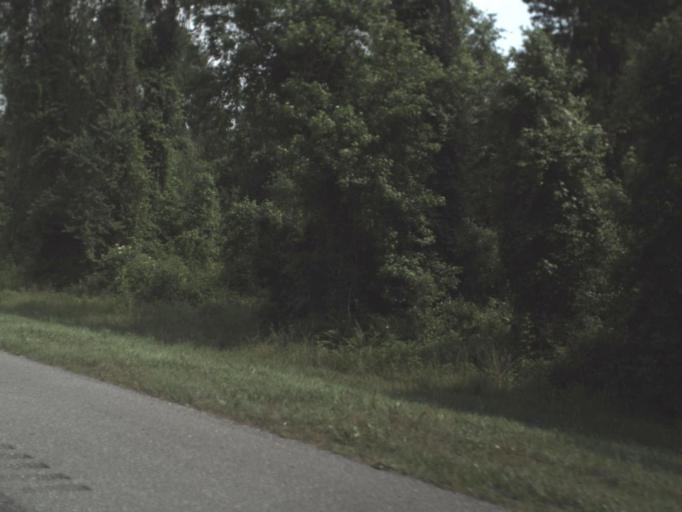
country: US
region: Florida
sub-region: Suwannee County
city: Live Oak
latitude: 30.3008
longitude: -82.9120
